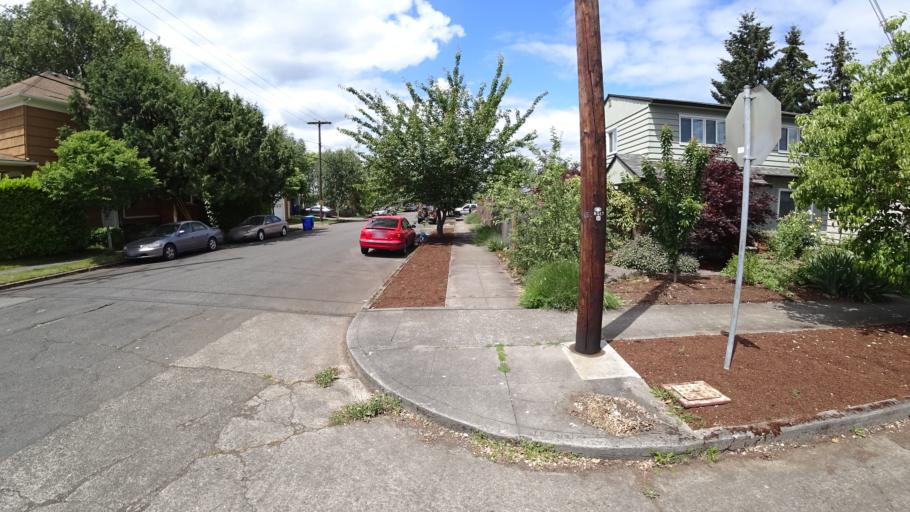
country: US
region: Oregon
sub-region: Multnomah County
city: Portland
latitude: 45.5851
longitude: -122.7241
